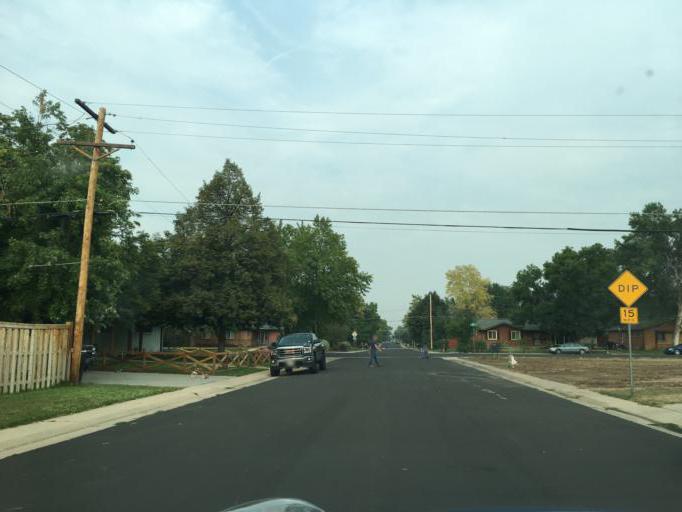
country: US
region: Colorado
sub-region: Arapahoe County
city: Glendale
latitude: 39.6875
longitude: -104.9303
